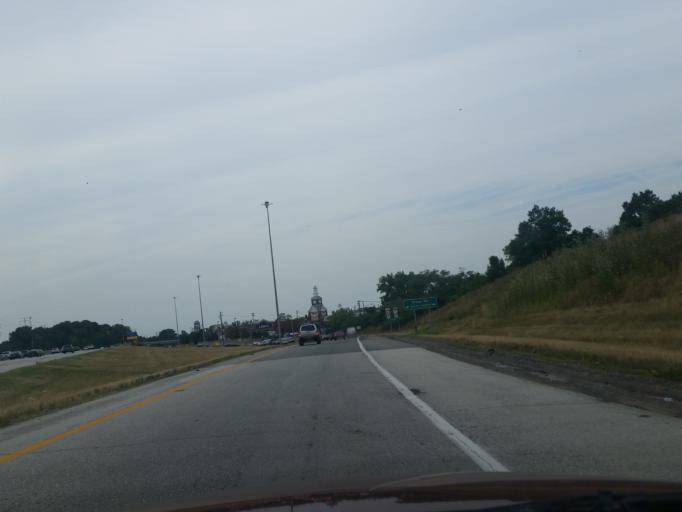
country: US
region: Ohio
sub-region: Cuyahoga County
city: Brooklyn
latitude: 41.4221
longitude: -81.7301
